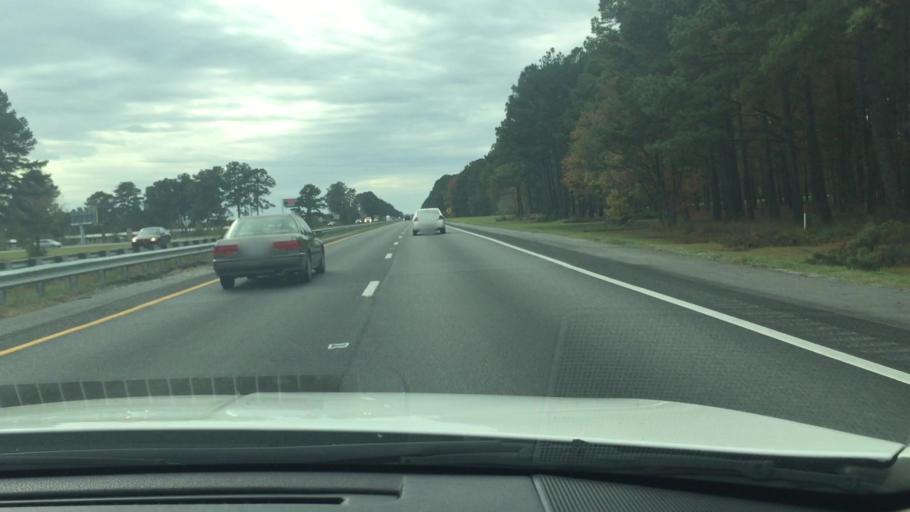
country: US
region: North Carolina
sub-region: Johnston County
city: Smithfield
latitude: 35.5040
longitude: -78.3215
